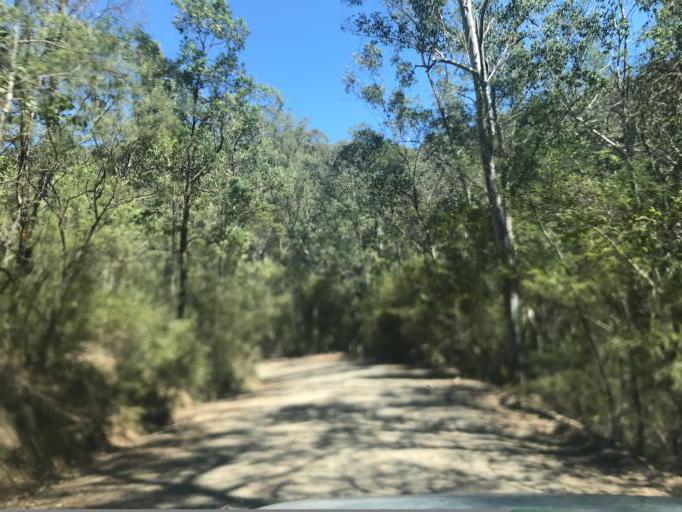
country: AU
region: New South Wales
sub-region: Wyong Shire
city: Little Jilliby
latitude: -33.1737
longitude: 151.0667
